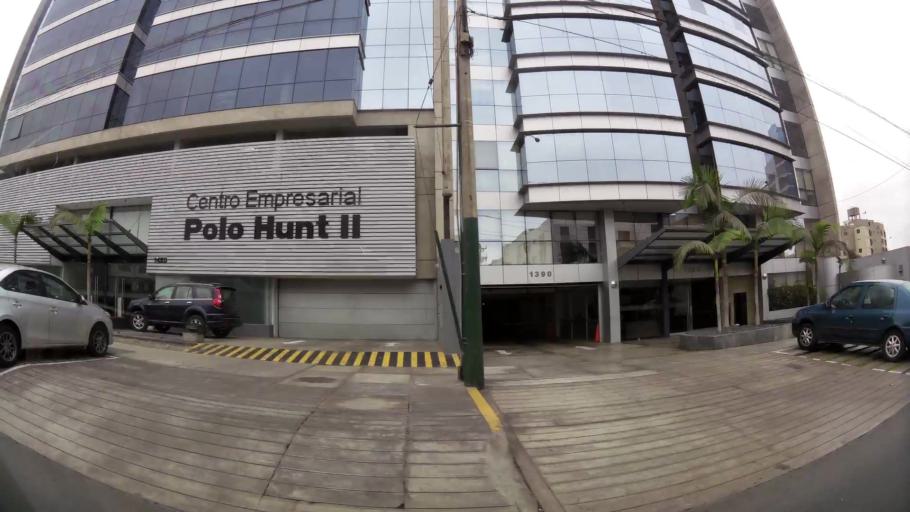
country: PE
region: Lima
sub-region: Lima
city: La Molina
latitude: -12.1026
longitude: -76.9705
